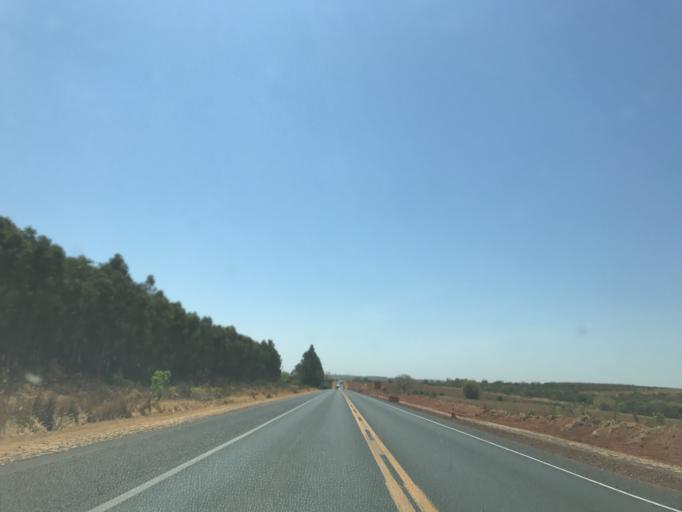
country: BR
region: Minas Gerais
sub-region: Prata
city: Prata
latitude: -19.3895
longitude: -48.8971
